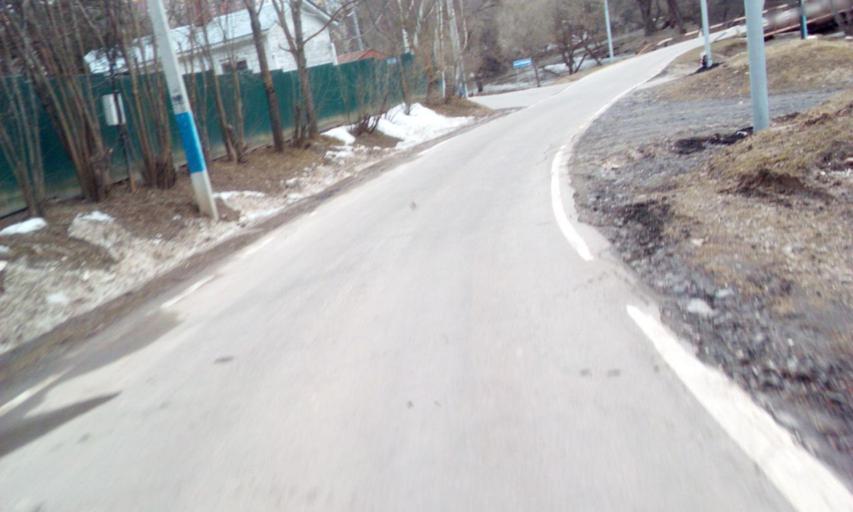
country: RU
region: Moskovskaya
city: Filimonki
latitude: 55.5242
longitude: 37.3630
